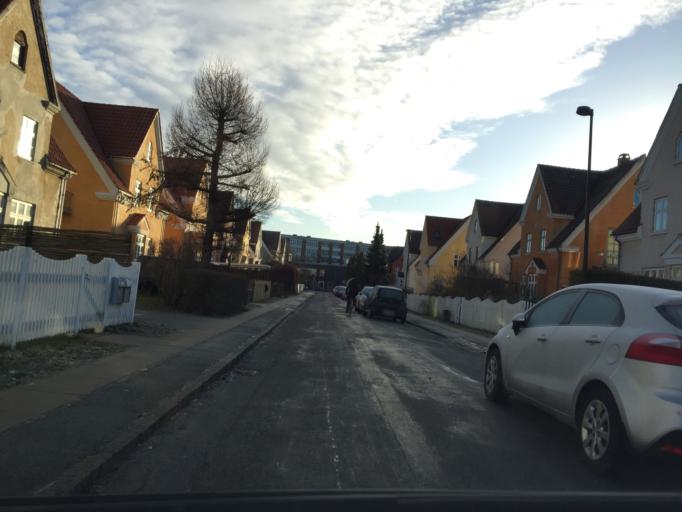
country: DK
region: Capital Region
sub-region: Kobenhavn
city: Vanlose
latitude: 55.6629
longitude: 12.5046
